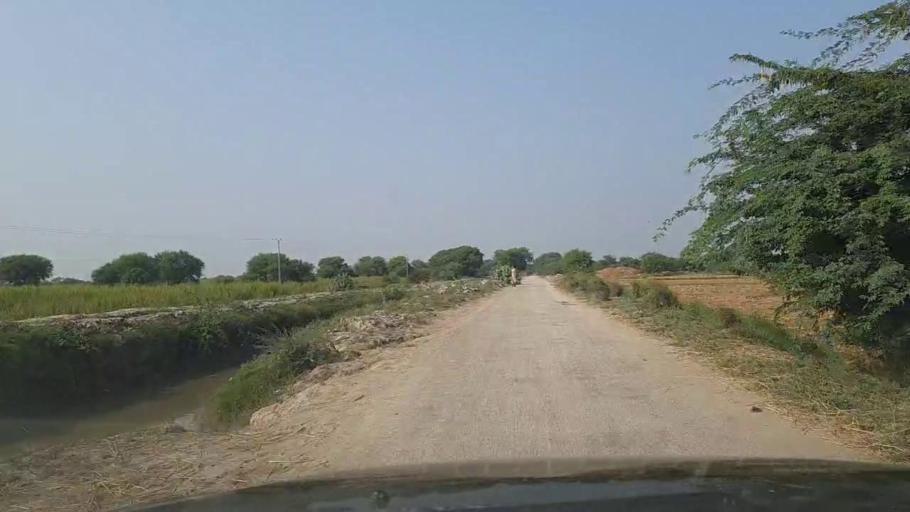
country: PK
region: Sindh
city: Mirpur Batoro
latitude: 24.7015
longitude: 68.2563
